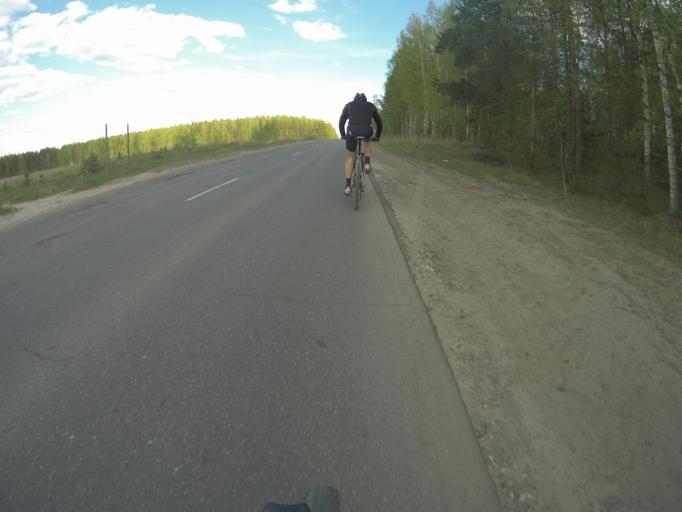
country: RU
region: Vladimir
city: Raduzhnyy
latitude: 55.9883
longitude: 40.2227
